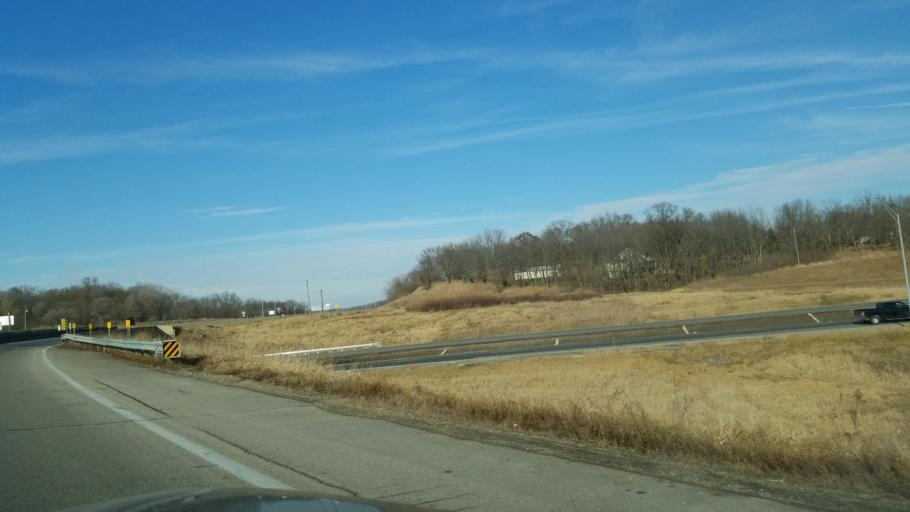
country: US
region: Iowa
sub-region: Linn County
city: Ely
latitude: 41.9255
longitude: -91.5411
